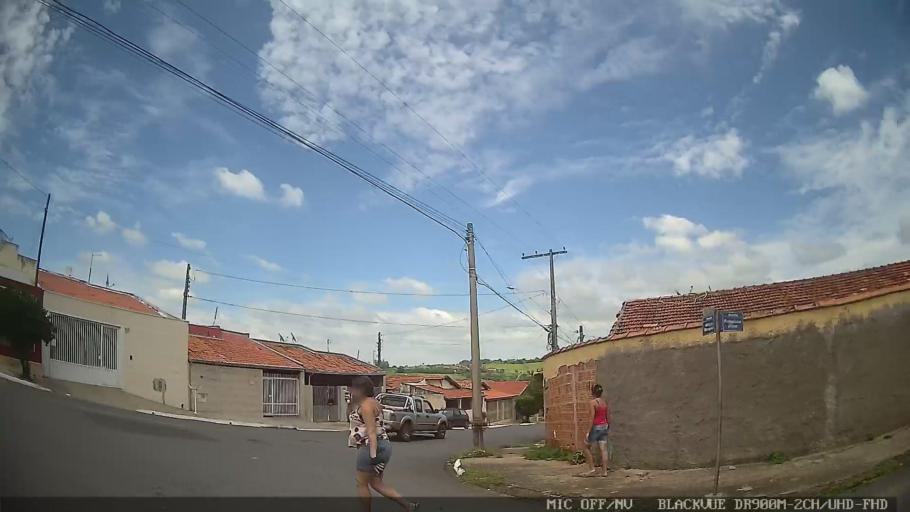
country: BR
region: Sao Paulo
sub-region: Laranjal Paulista
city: Laranjal Paulista
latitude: -23.0383
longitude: -47.8290
